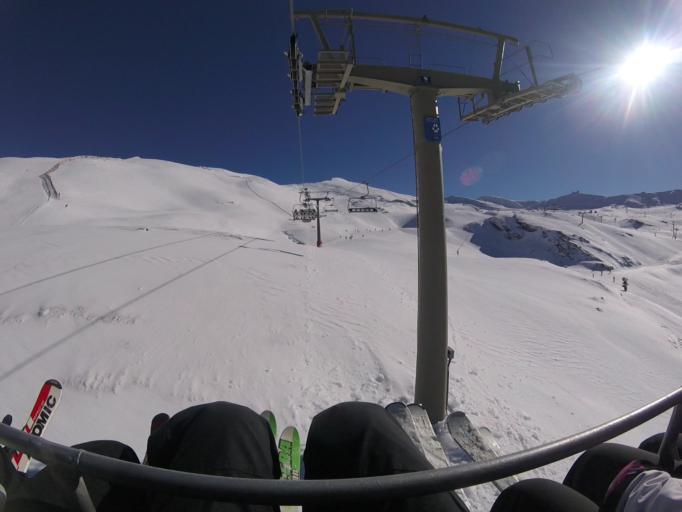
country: ES
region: Andalusia
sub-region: Provincia de Granada
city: Guejar-Sierra
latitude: 37.0736
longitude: -3.3850
